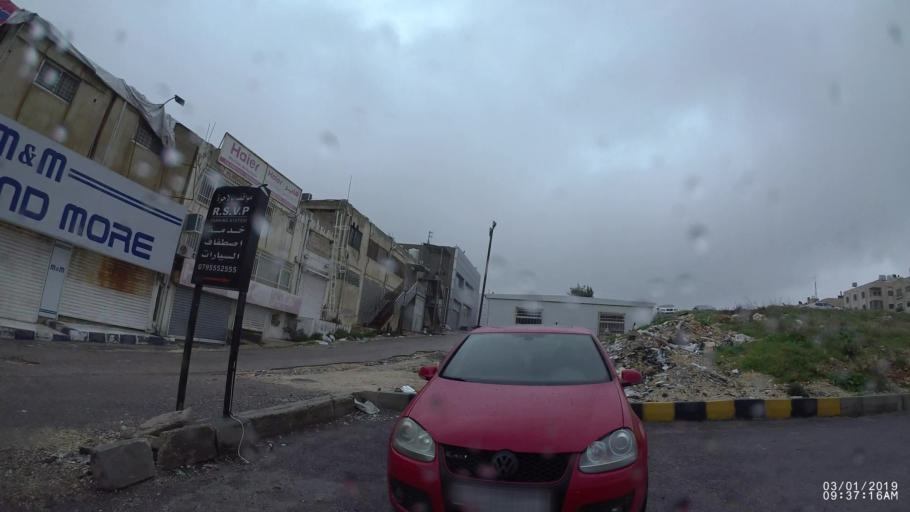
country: JO
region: Amman
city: Wadi as Sir
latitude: 31.9734
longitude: 35.8415
